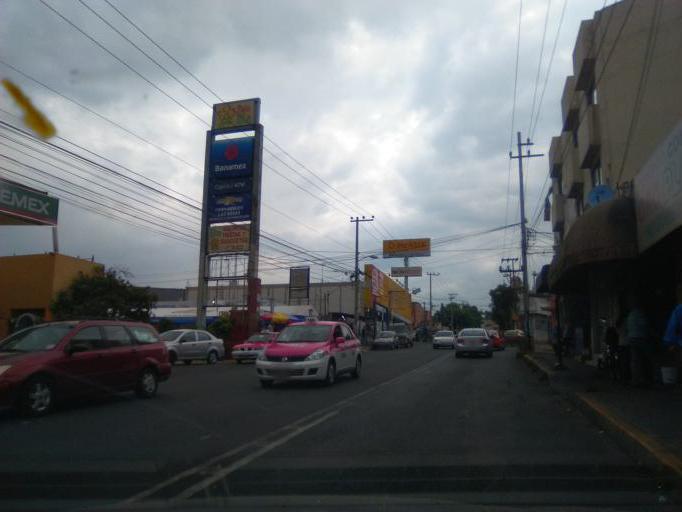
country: MX
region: Mexico City
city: Alvaro Obregon
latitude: 19.3729
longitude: -99.2070
